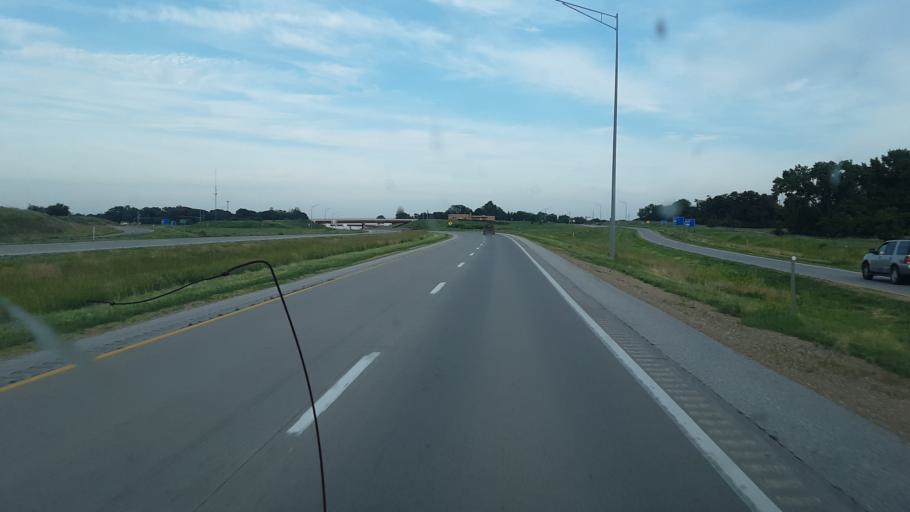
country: US
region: Iowa
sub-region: Tama County
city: Toledo
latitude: 41.9826
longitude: -92.5883
